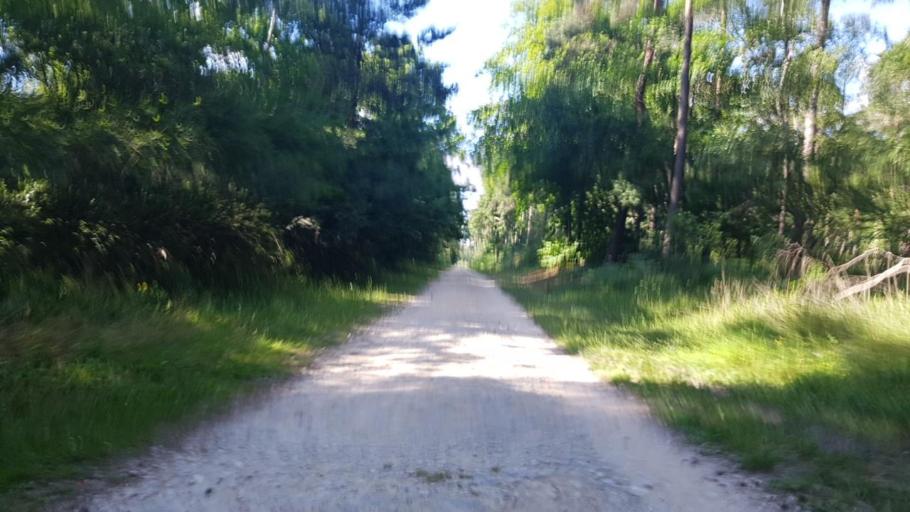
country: FR
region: Picardie
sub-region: Departement de l'Oise
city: Ver-sur-Launette
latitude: 49.1366
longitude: 2.6561
